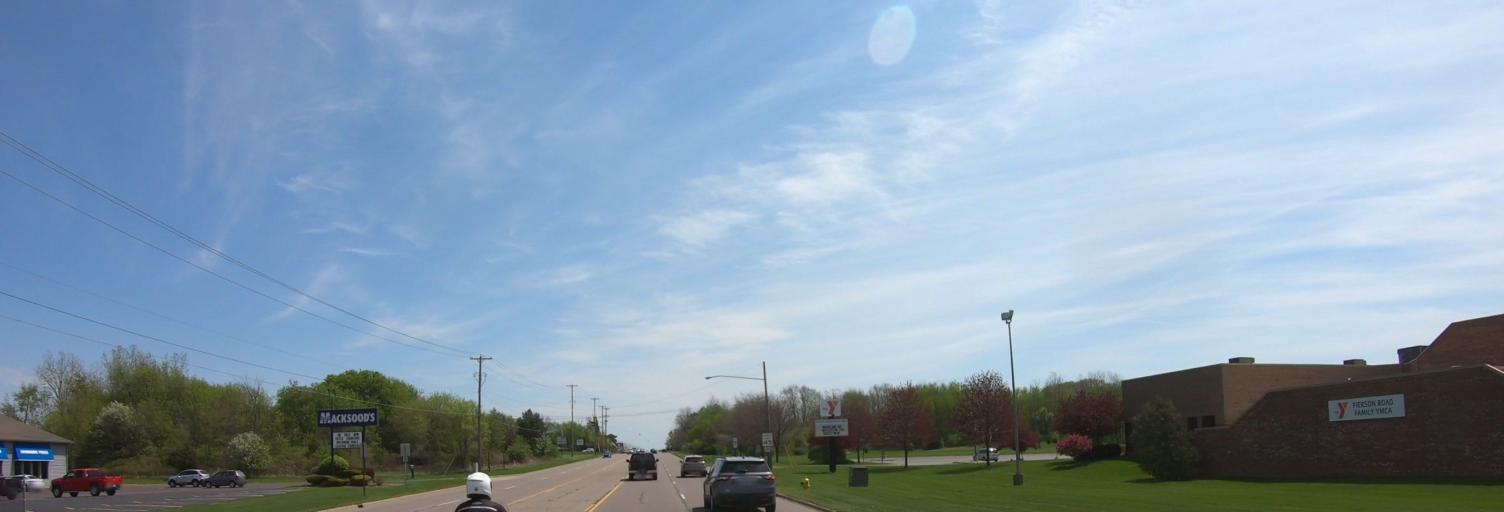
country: US
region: Michigan
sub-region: Genesee County
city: Flushing
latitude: 43.0604
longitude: -83.7814
